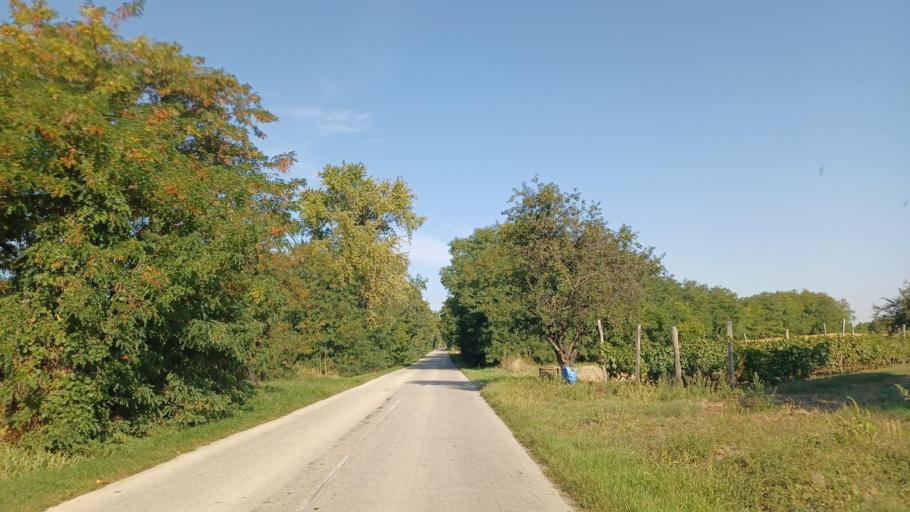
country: HU
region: Tolna
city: Dunaszentgyorgy
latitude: 46.5109
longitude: 18.7853
